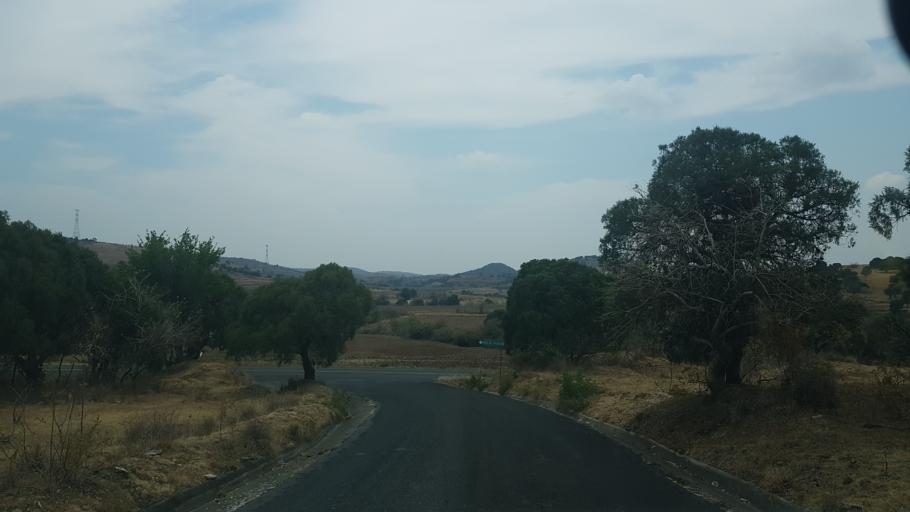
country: MX
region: Puebla
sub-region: Atzitzihuacan
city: Santiago Atzitzihuacan
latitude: 18.8330
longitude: -98.6163
